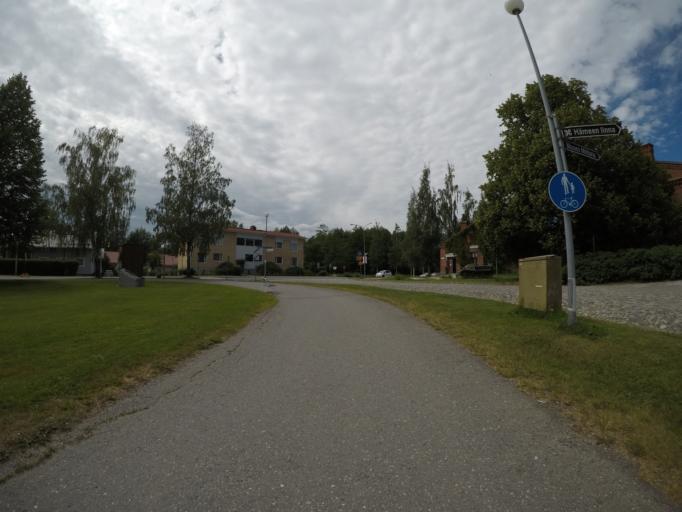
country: FI
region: Haeme
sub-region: Haemeenlinna
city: Haemeenlinna
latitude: 61.0035
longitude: 24.4563
